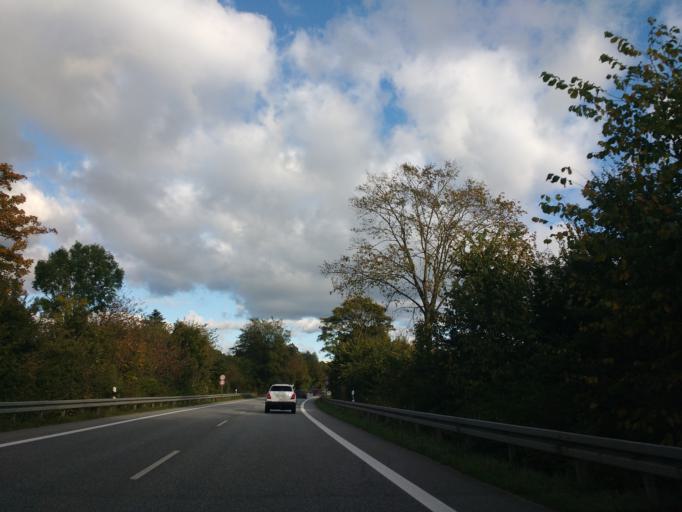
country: DE
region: Schleswig-Holstein
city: Schashagen
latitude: 54.1262
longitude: 10.8835
